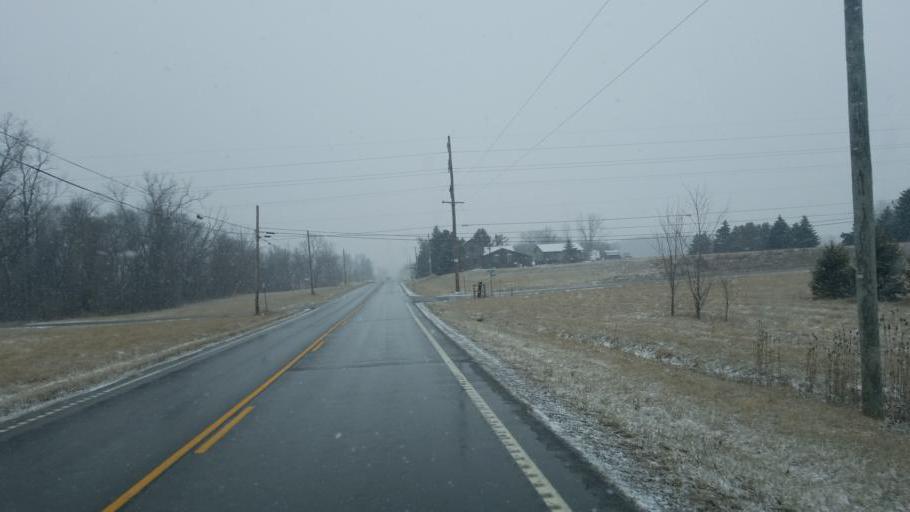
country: US
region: Ohio
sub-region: Defiance County
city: Hicksville
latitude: 41.3531
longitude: -84.7479
